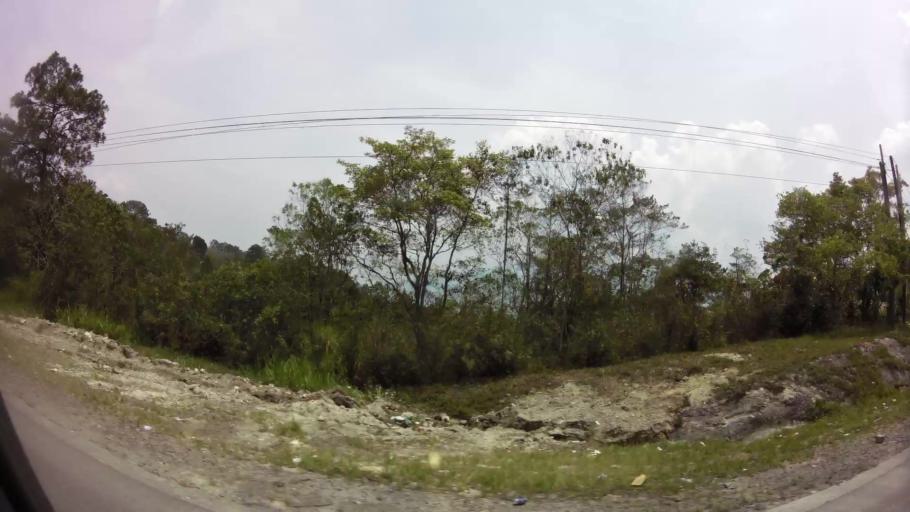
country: HN
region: Comayagua
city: El Socorro
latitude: 14.6472
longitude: -87.9332
